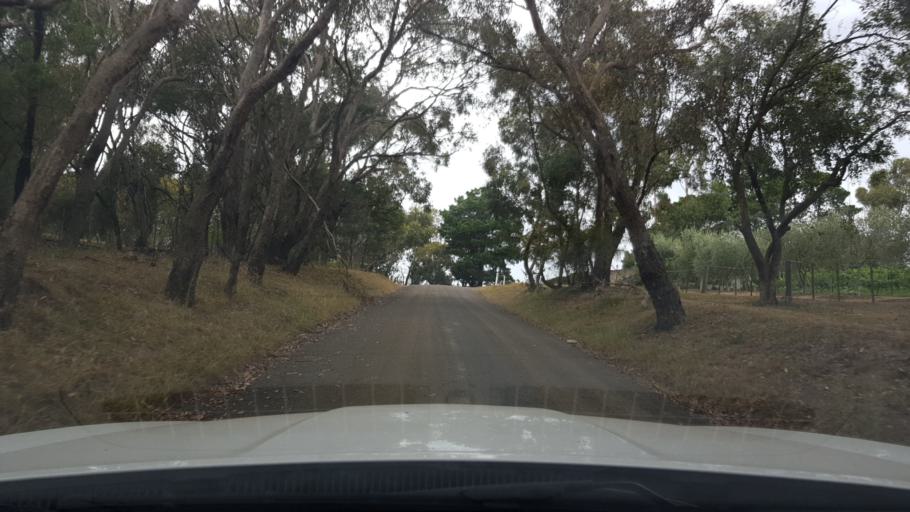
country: AU
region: Victoria
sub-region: Whittlesea
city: Whittlesea
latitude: -37.4846
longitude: 145.0369
